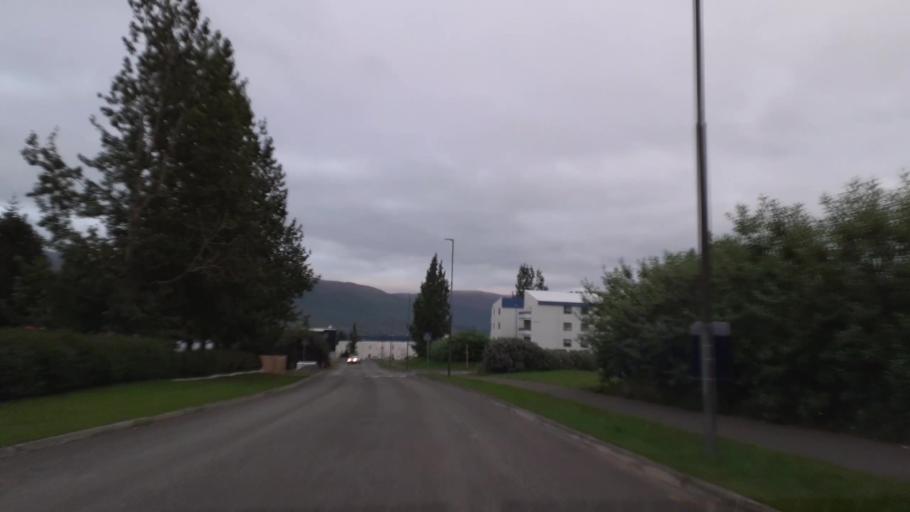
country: IS
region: Northeast
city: Akureyri
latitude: 65.6947
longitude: -18.1362
